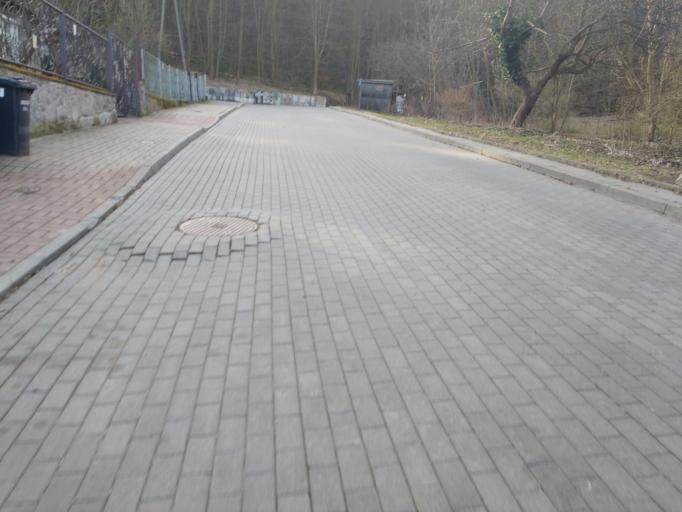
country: PL
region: Pomeranian Voivodeship
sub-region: Gdynia
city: Wielki Kack
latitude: 54.4827
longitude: 18.5162
